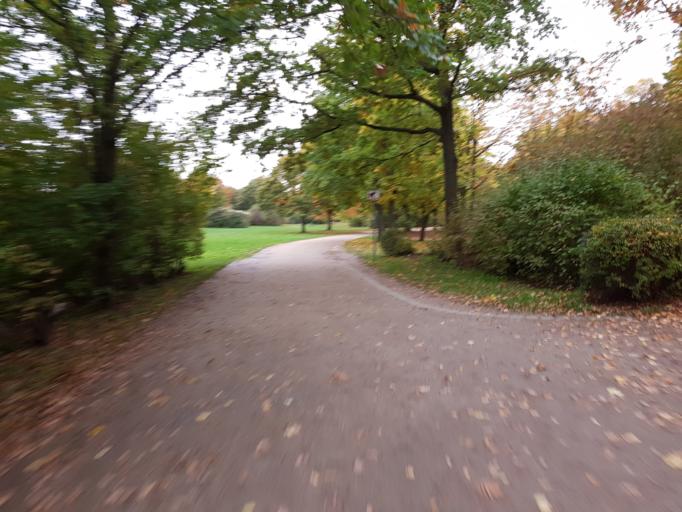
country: DE
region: Hesse
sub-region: Regierungsbezirk Darmstadt
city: Frankfurt am Main
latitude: 50.1454
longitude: 8.6731
